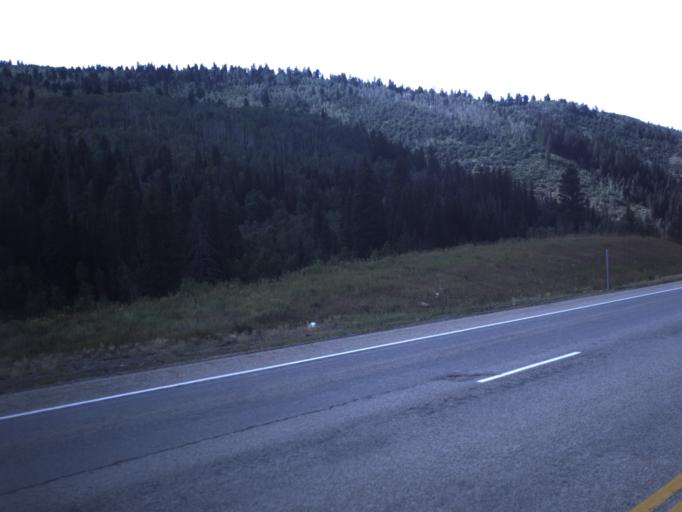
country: US
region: Utah
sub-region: Wasatch County
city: Heber
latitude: 40.3199
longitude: -111.2587
